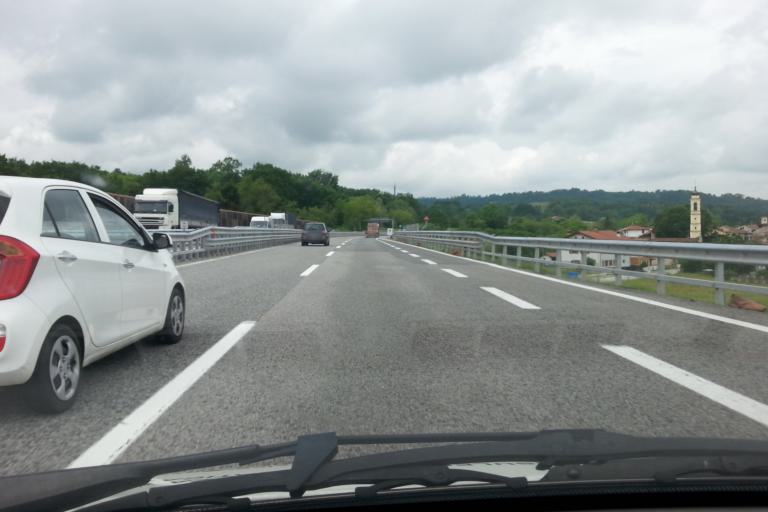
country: IT
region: Piedmont
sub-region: Provincia di Cuneo
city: Borgo
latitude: 44.4044
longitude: 7.9341
